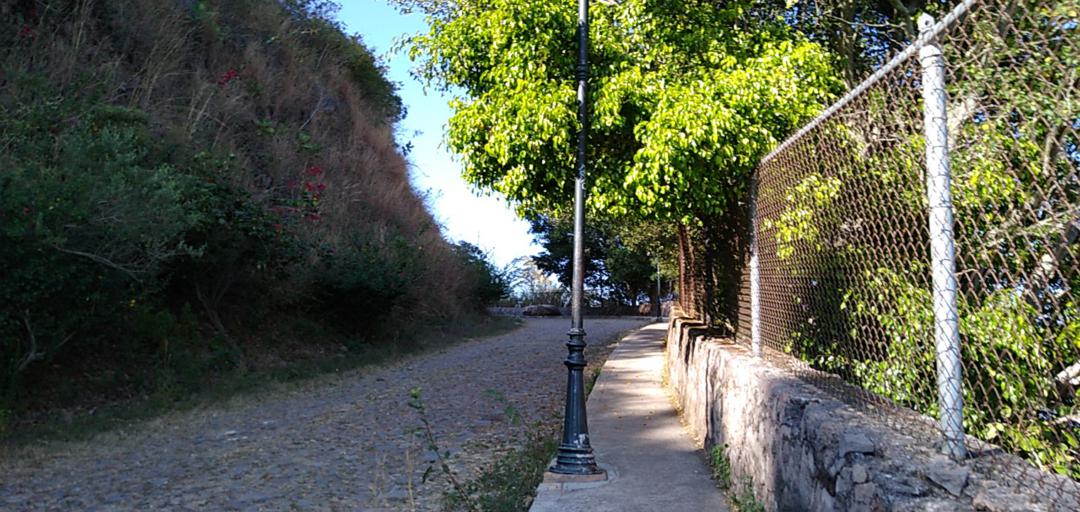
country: MX
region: Nayarit
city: Tepic
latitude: 21.5343
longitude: -104.8835
